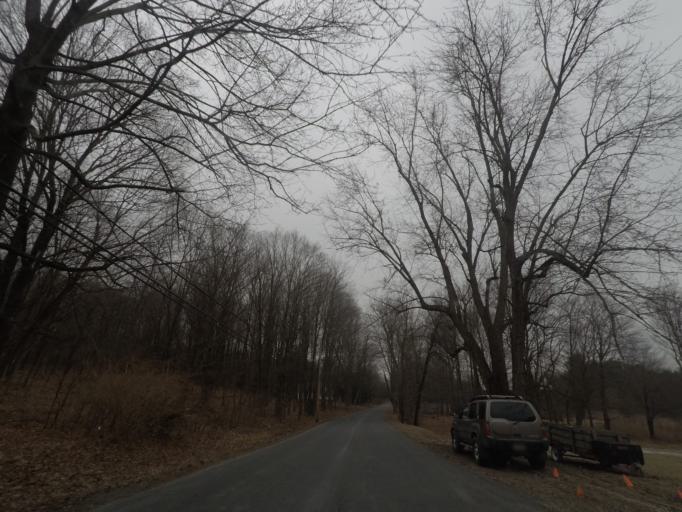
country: US
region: New York
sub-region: Rensselaer County
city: East Greenbush
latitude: 42.5768
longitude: -73.6706
